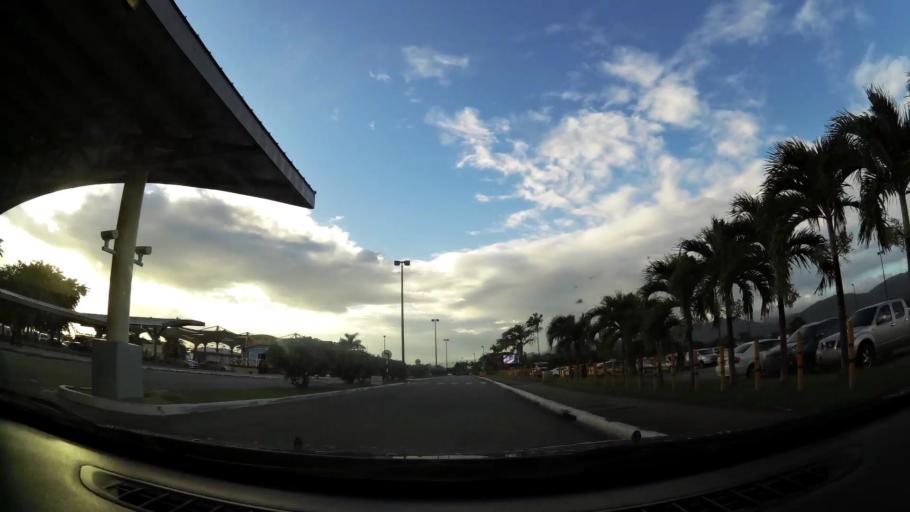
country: TT
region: Tunapuna/Piarco
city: Arouca
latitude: 10.6025
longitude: -61.3406
